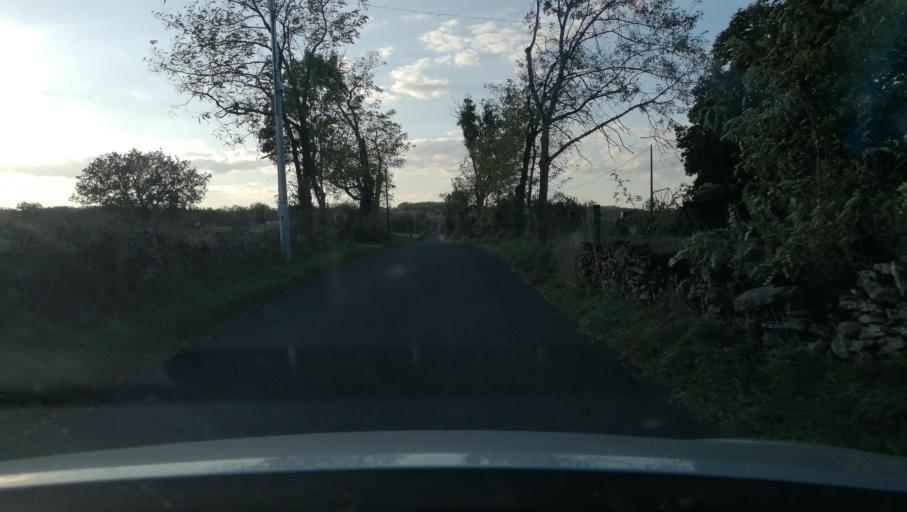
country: FR
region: Midi-Pyrenees
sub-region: Departement du Lot
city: Vayrac
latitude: 44.8712
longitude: 1.6335
